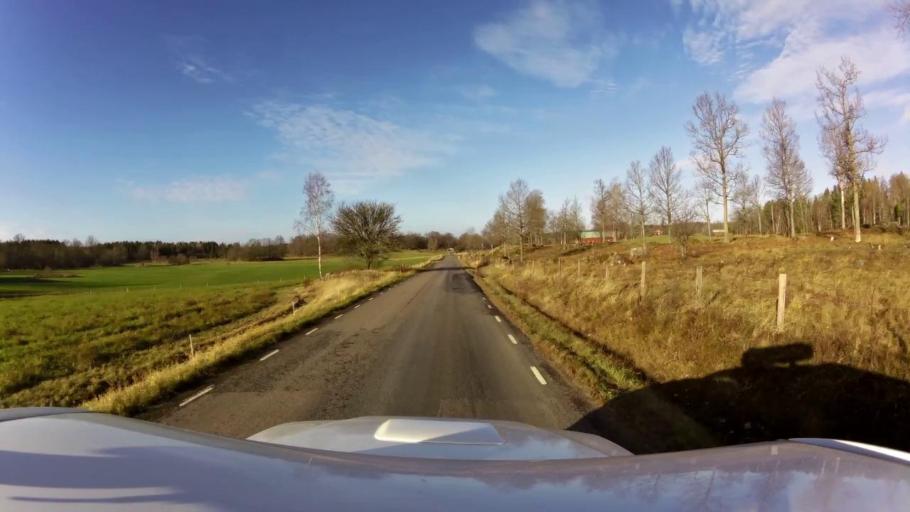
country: SE
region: OEstergoetland
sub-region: Linkopings Kommun
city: Linkoping
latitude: 58.3411
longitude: 15.6493
